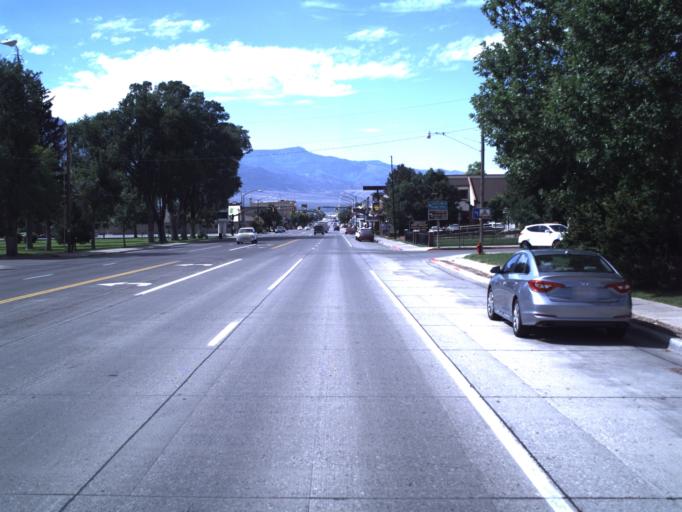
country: US
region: Utah
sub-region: Sevier County
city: Richfield
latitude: 38.7743
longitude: -112.0849
